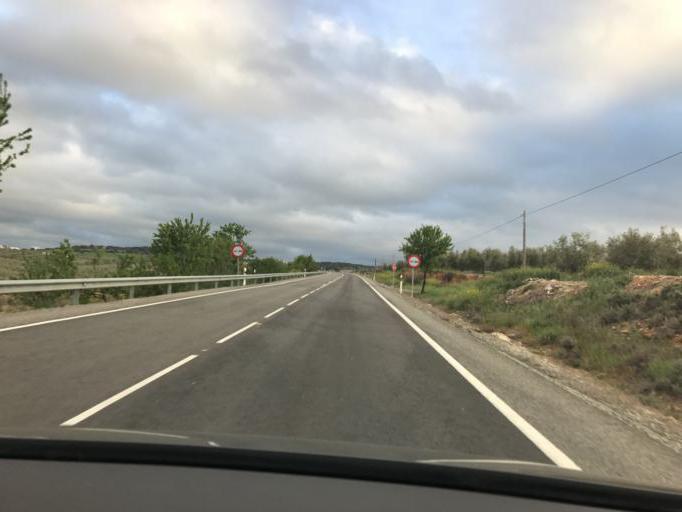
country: ES
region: Andalusia
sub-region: Provincia de Jaen
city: Guadahortuna
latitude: 37.5416
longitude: -3.3868
